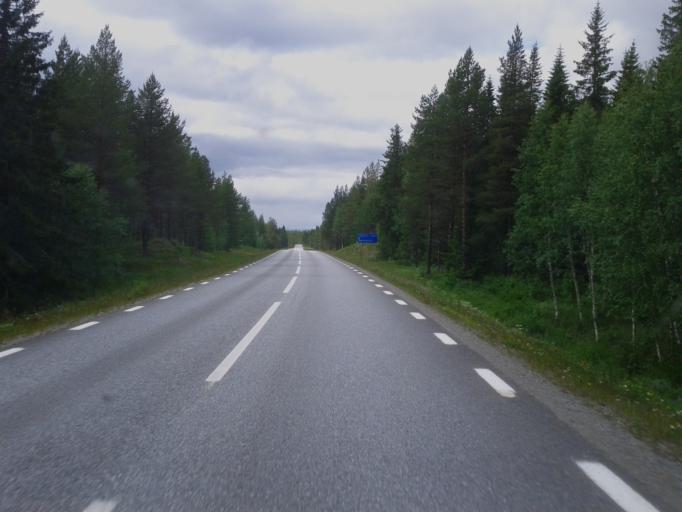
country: SE
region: Vaesterbotten
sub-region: Storumans Kommun
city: Fristad
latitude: 65.3975
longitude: 16.4382
